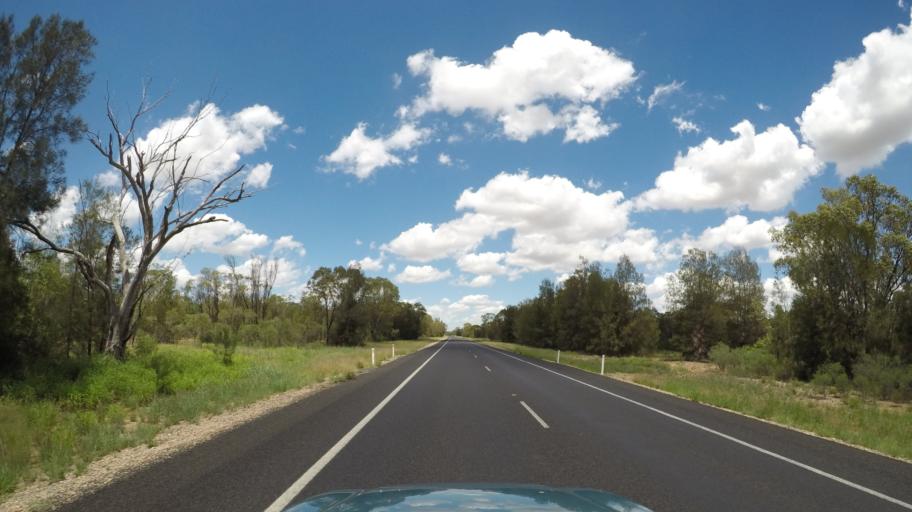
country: AU
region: Queensland
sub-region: Goondiwindi
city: Goondiwindi
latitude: -28.0641
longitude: 150.7607
